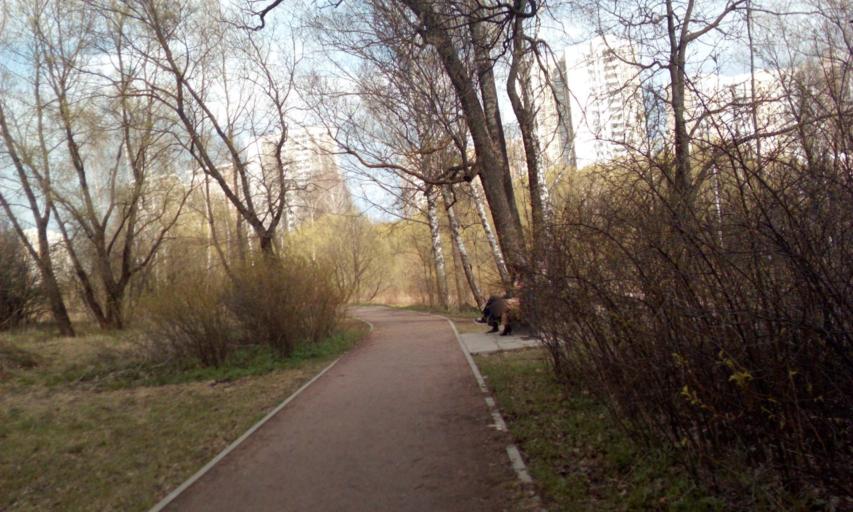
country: RU
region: Moscow
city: Novo-Peredelkino
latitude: 55.6470
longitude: 37.3338
